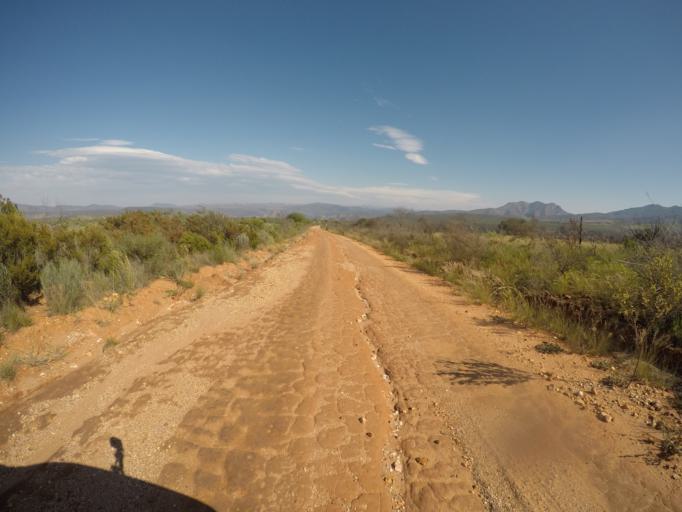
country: ZA
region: Eastern Cape
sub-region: Cacadu District Municipality
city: Kareedouw
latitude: -33.6356
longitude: 24.4618
